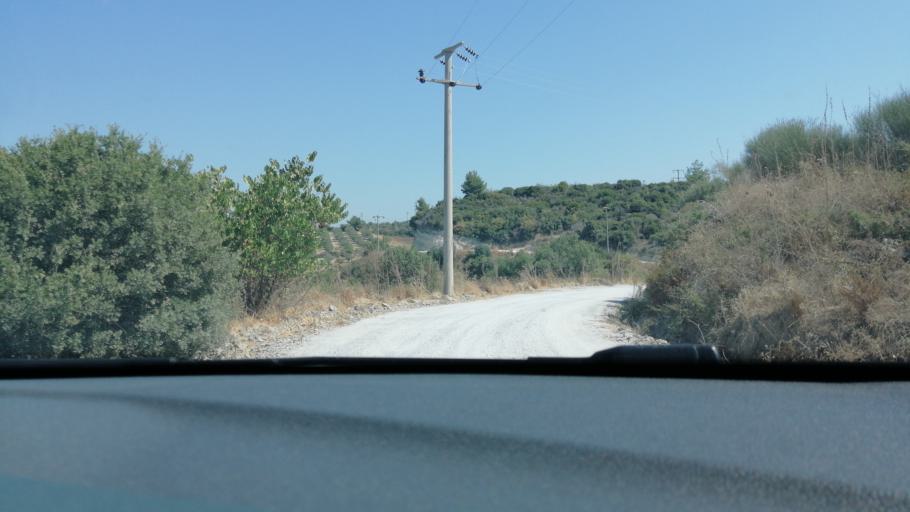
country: TR
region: Aydin
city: Davutlar
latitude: 37.7813
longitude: 27.3132
